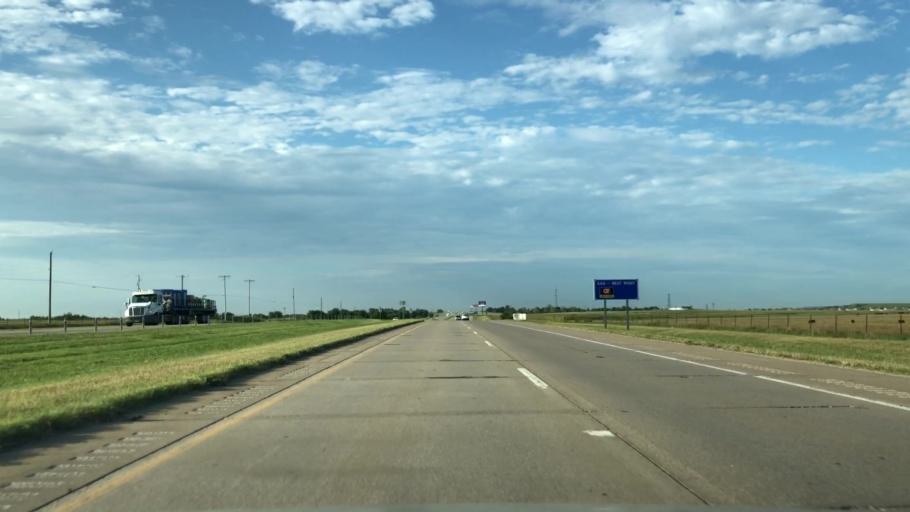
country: US
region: Oklahoma
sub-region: Osage County
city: Skiatook
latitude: 36.3816
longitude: -95.9204
